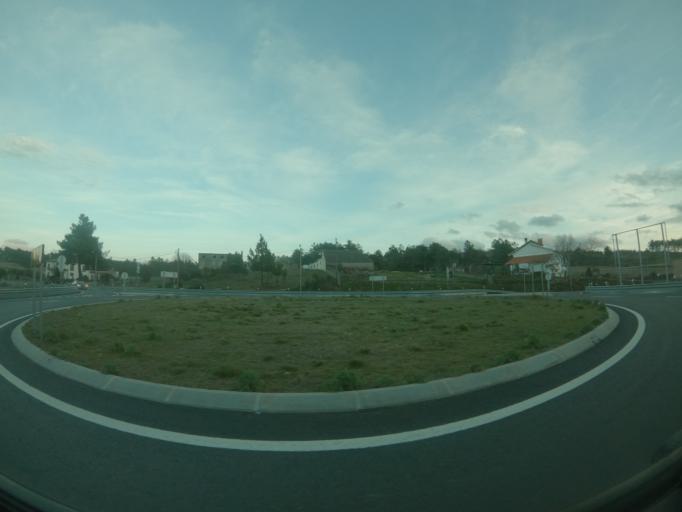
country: PT
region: Braganca
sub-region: Carrazeda de Ansiaes
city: Carrazeda de Anciaes
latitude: 41.2527
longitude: -7.2845
